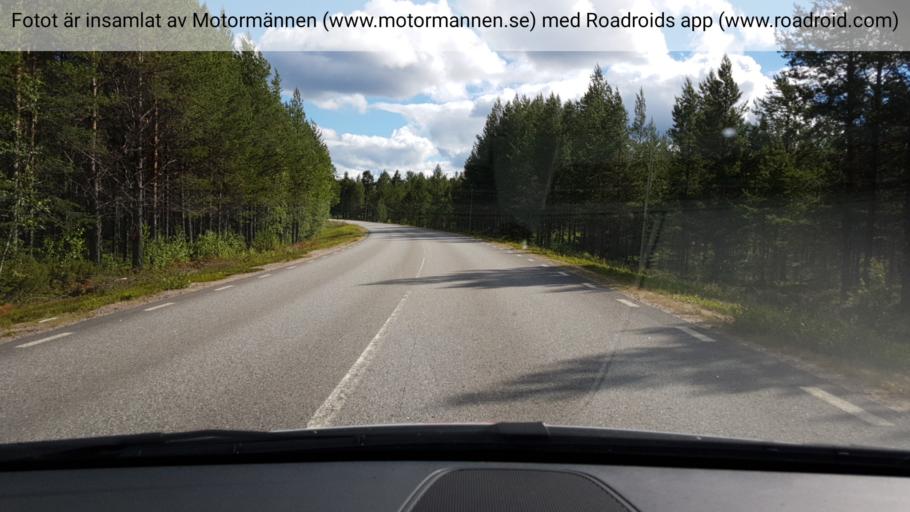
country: SE
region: Jaemtland
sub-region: Harjedalens Kommun
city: Sveg
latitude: 62.0415
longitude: 14.6392
